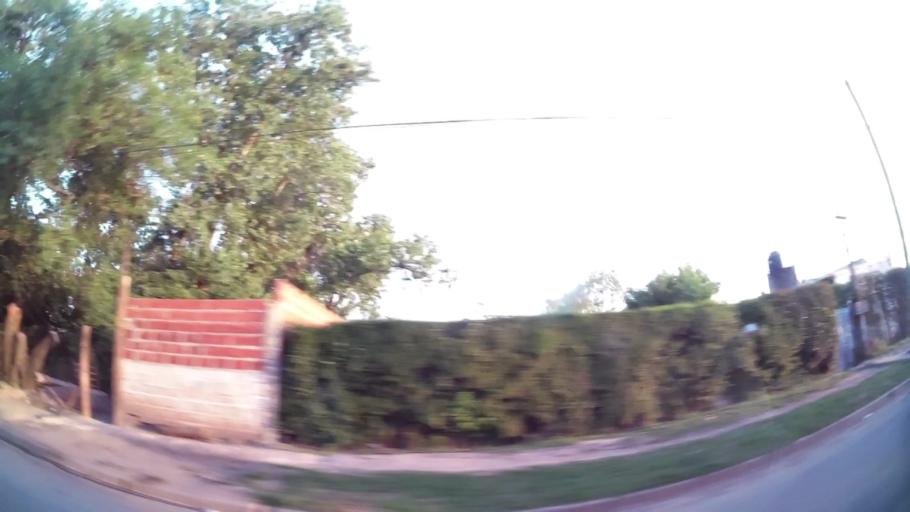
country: AR
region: Buenos Aires
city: Santa Catalina - Dique Lujan
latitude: -34.4890
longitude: -58.7532
